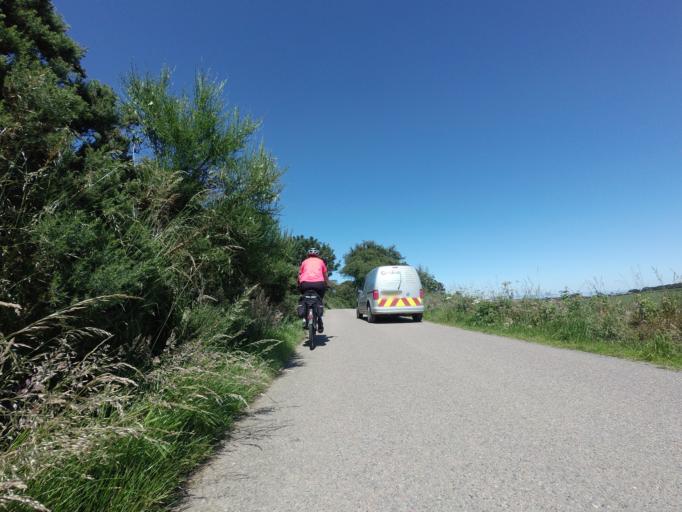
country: GB
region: Scotland
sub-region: Aberdeenshire
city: Macduff
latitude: 57.6491
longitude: -2.5043
